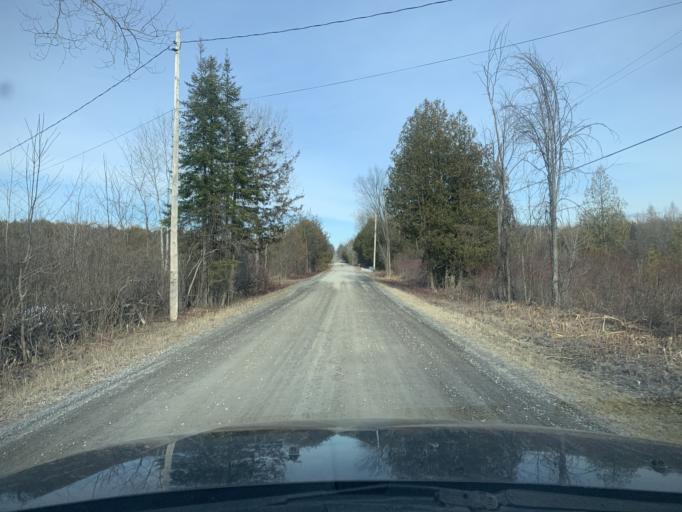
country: CA
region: Ontario
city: Deseronto
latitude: 44.3973
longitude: -77.1444
